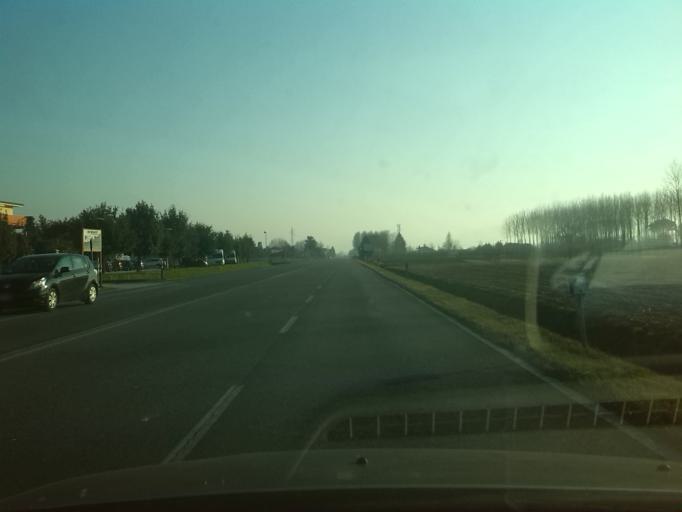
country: IT
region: Friuli Venezia Giulia
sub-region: Provincia di Udine
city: Pertegada
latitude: 45.7441
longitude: 13.0372
